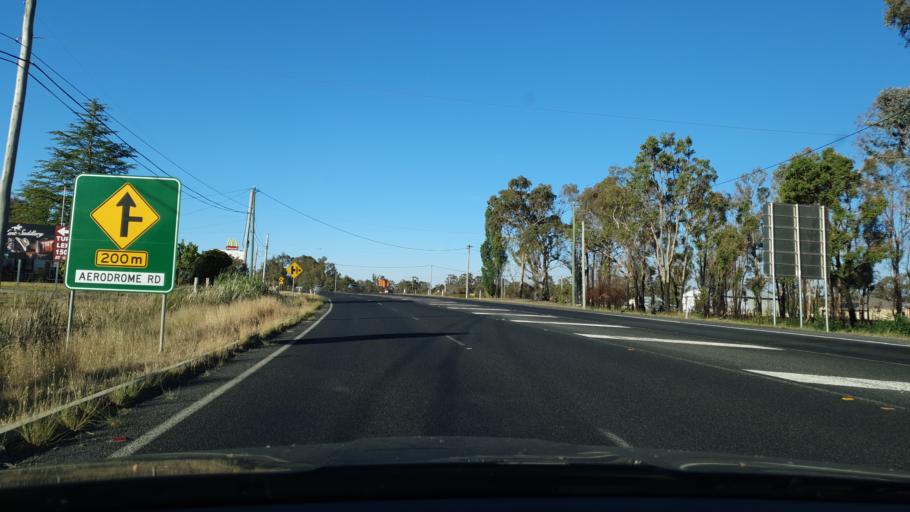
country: AU
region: Queensland
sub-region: Southern Downs
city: Stanthorpe
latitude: -28.6334
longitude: 151.9533
